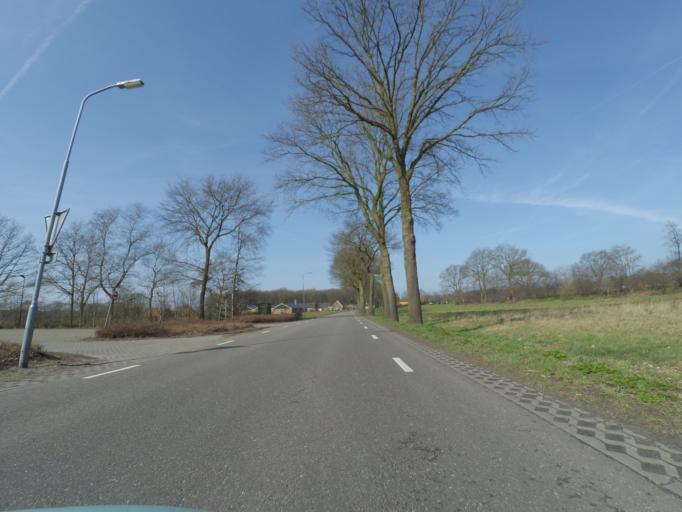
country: NL
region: Gelderland
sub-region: Gemeente Putten
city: Putten
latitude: 52.2232
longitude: 5.6050
